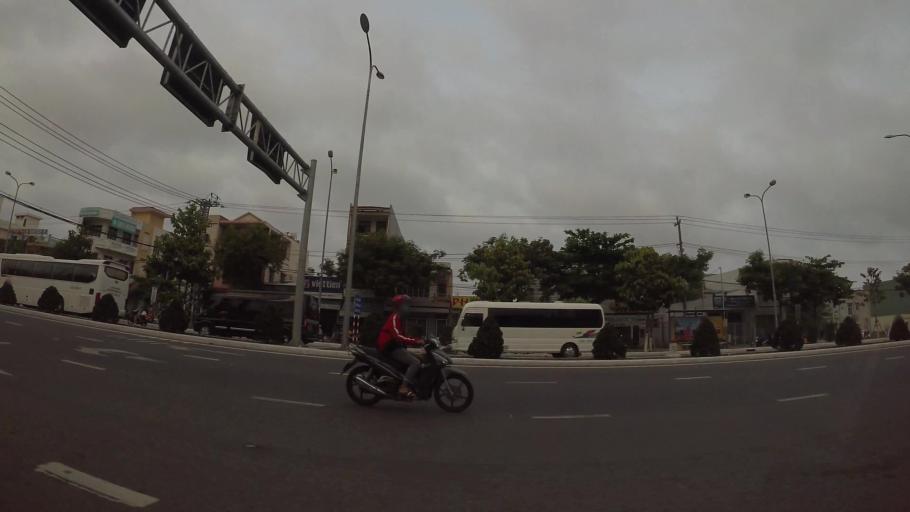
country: VN
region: Da Nang
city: Son Tra
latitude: 16.0398
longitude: 108.2421
